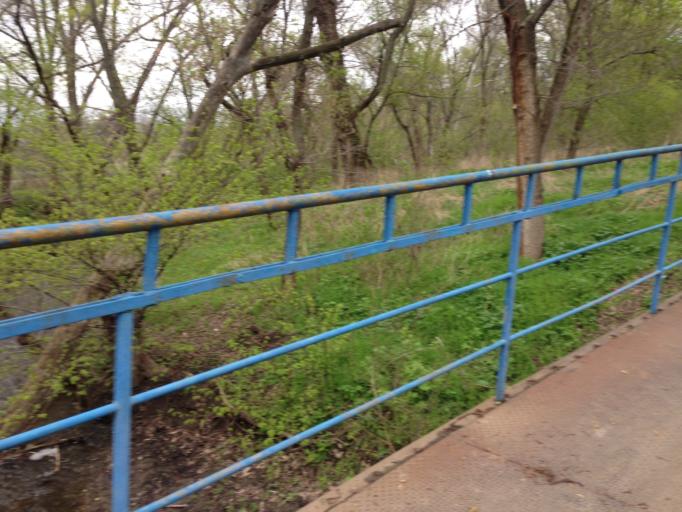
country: RU
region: Rostov
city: Kamensk-Shakhtinskiy
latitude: 48.3327
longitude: 40.2493
